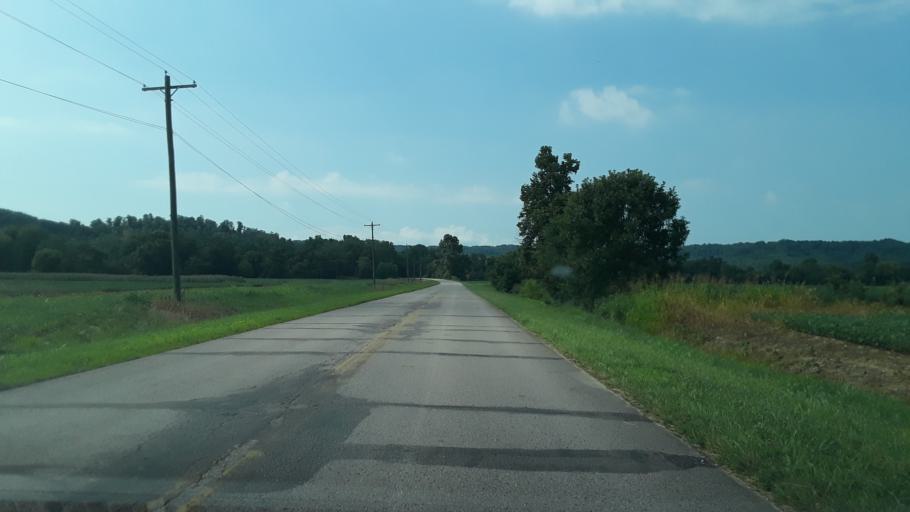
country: US
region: Indiana
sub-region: Clark County
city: Sellersburg
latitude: 38.4526
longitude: -85.8655
